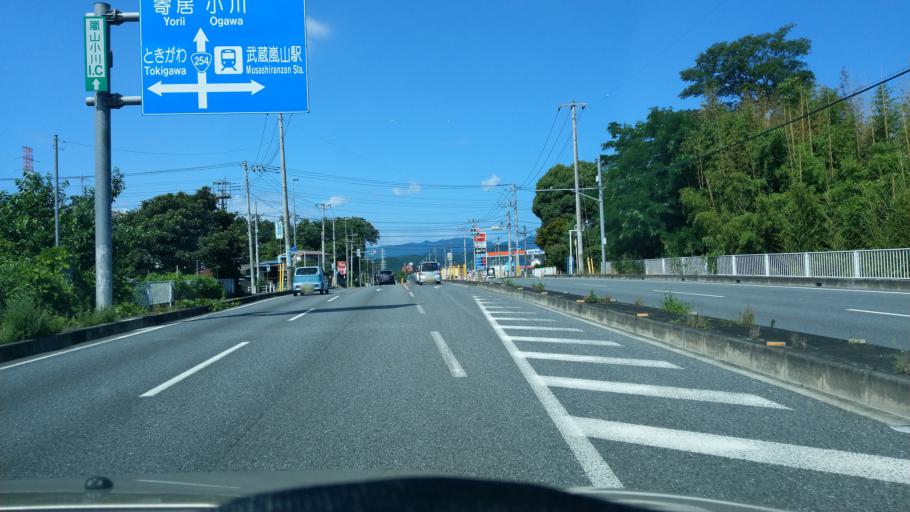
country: JP
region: Saitama
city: Ogawa
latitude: 36.0386
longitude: 139.3366
